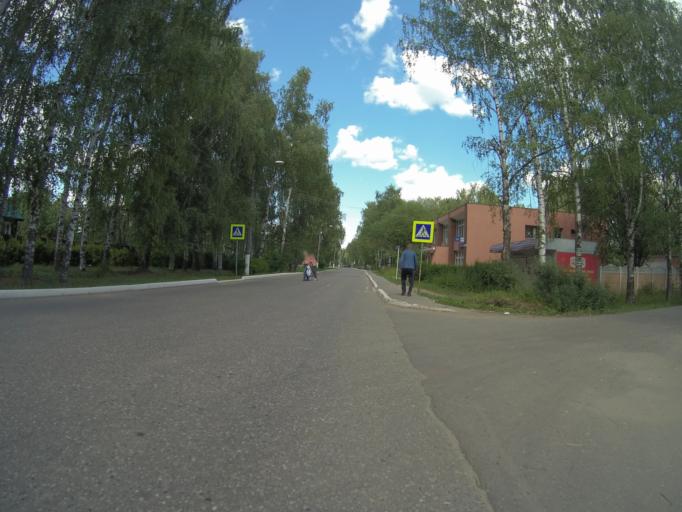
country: RU
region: Ivanovo
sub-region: Privolzhskiy Rayon
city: Ples
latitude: 57.4532
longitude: 41.5067
